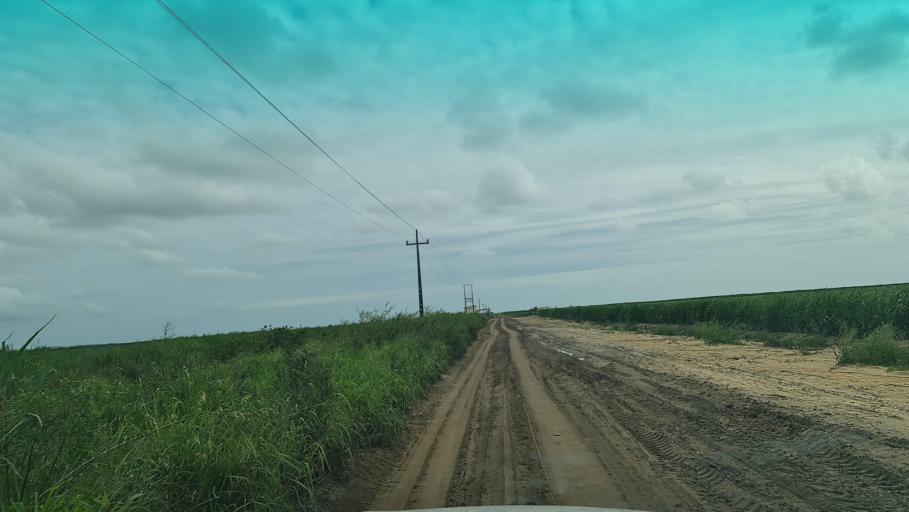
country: MZ
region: Maputo
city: Manhica
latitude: -25.4520
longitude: 32.8391
